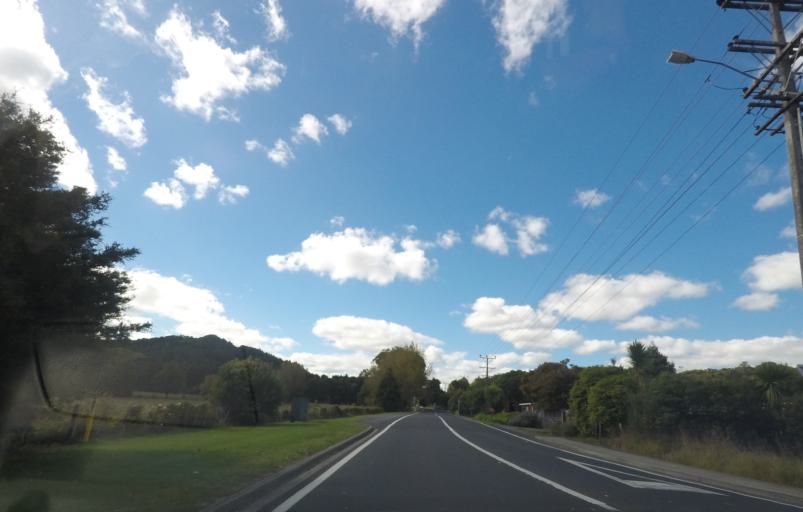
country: NZ
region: Auckland
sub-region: Auckland
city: Parakai
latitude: -36.6344
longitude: 174.5513
